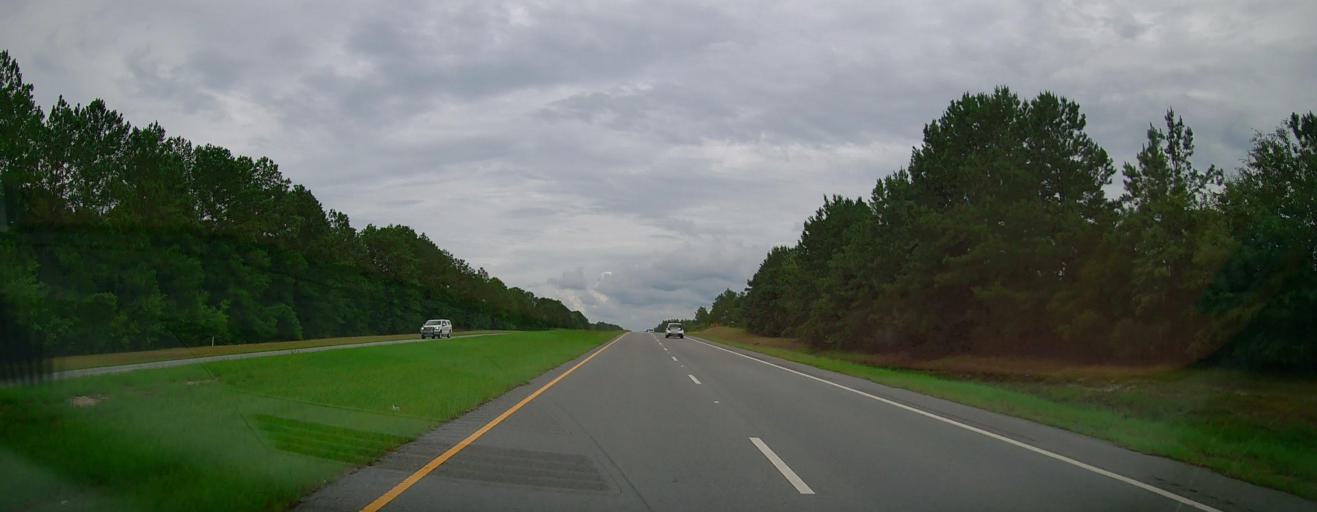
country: US
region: Georgia
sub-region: Telfair County
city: Helena
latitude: 32.0956
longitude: -82.9479
